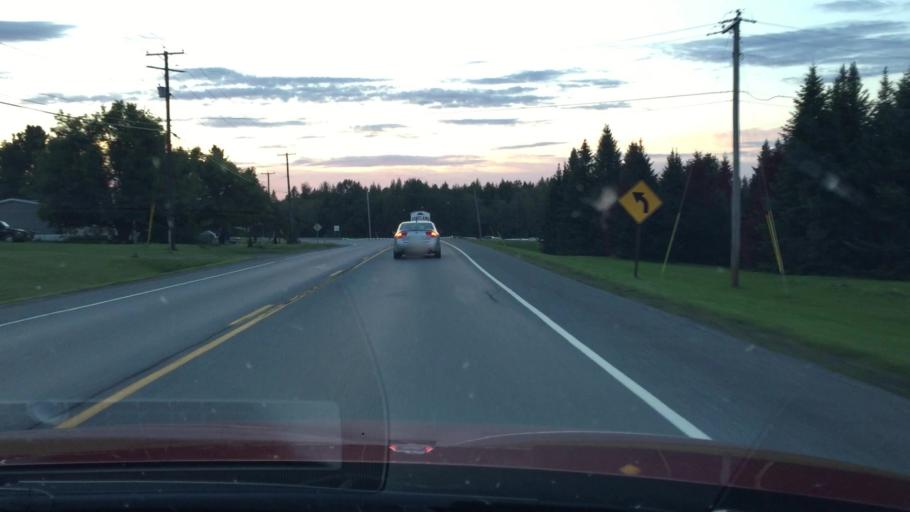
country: US
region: Maine
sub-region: Aroostook County
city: Easton
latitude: 46.5246
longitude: -67.8782
